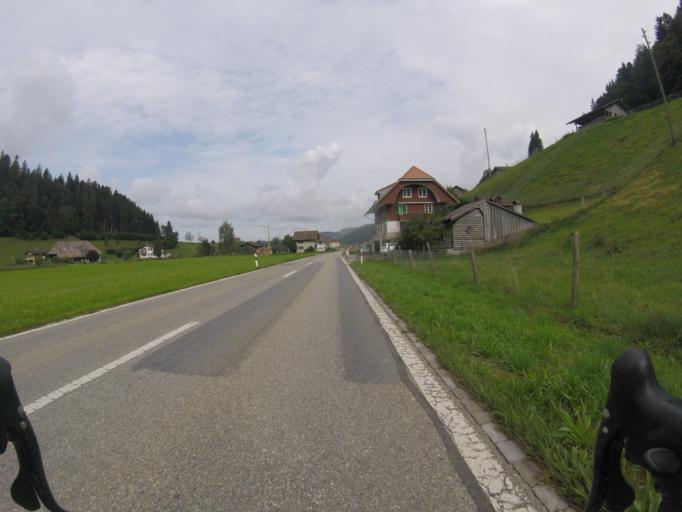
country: CH
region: Bern
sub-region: Emmental District
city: Lutzelfluh
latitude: 46.9974
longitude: 7.6811
